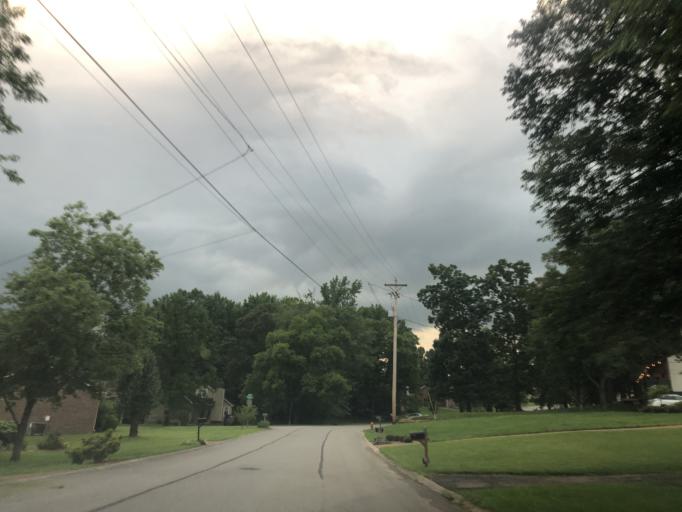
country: US
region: Tennessee
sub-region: Davidson County
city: Lakewood
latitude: 36.1487
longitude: -86.6294
